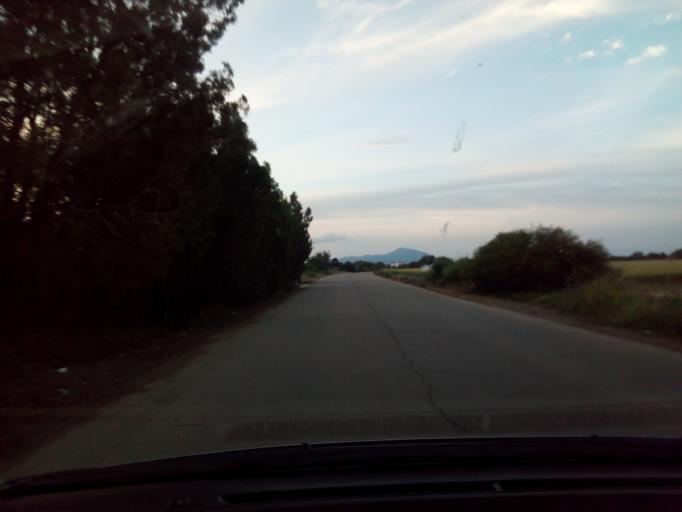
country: CY
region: Larnaka
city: Tersefanou
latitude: 34.7973
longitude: 33.5123
